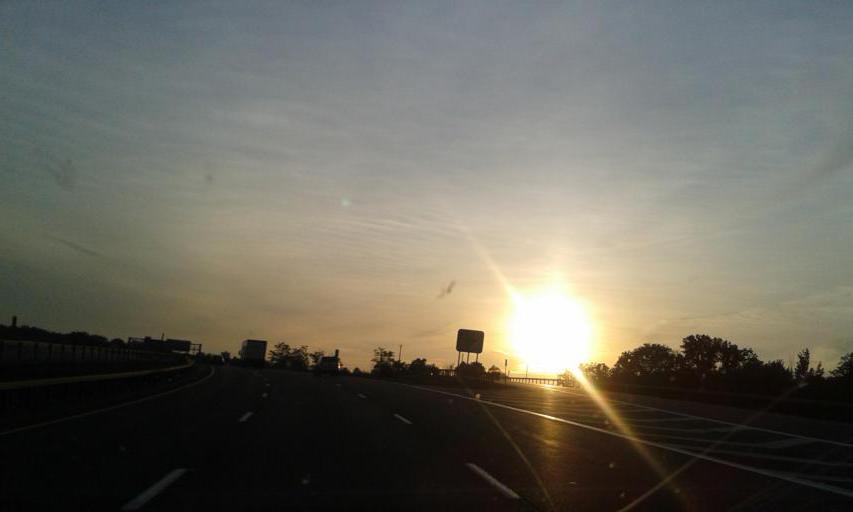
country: US
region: New York
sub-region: Onondaga County
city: Lakeland
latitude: 43.1063
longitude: -76.2482
